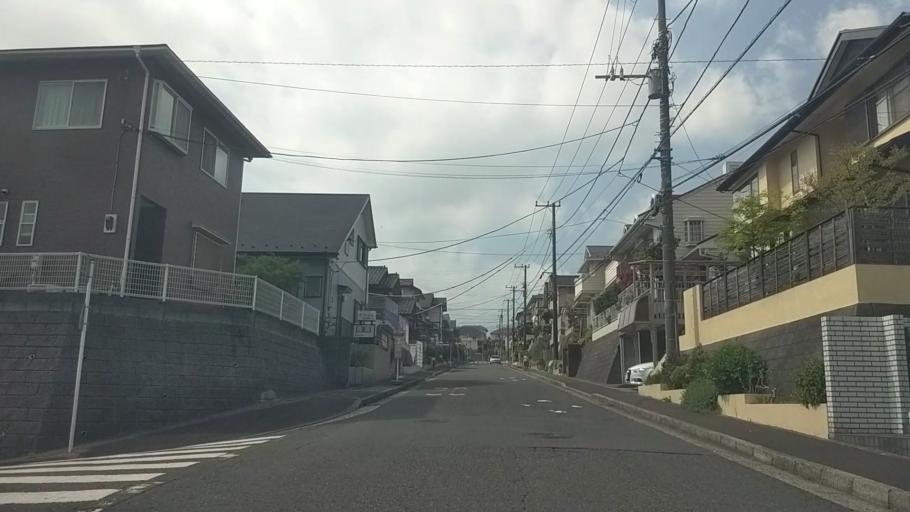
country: JP
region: Kanagawa
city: Yokohama
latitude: 35.3806
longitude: 139.6059
